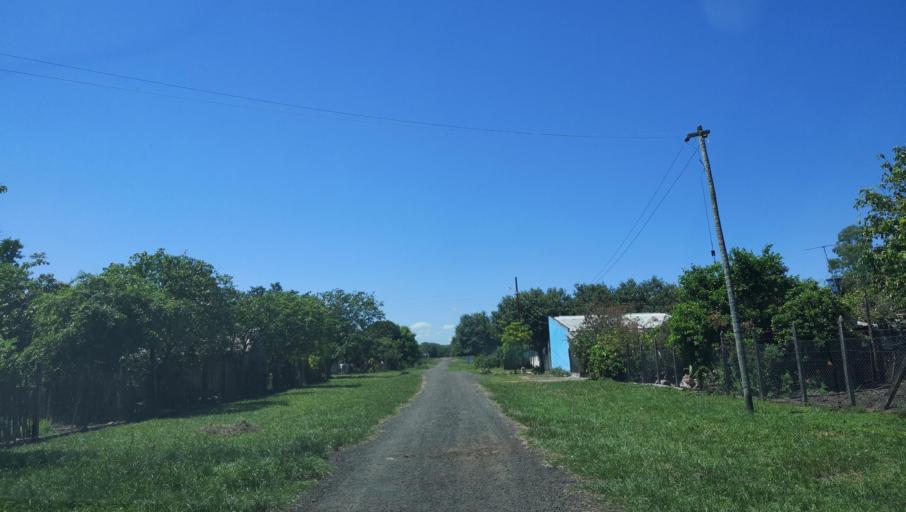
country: PY
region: Caaguazu
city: Carayao
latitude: -25.2012
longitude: -56.4018
